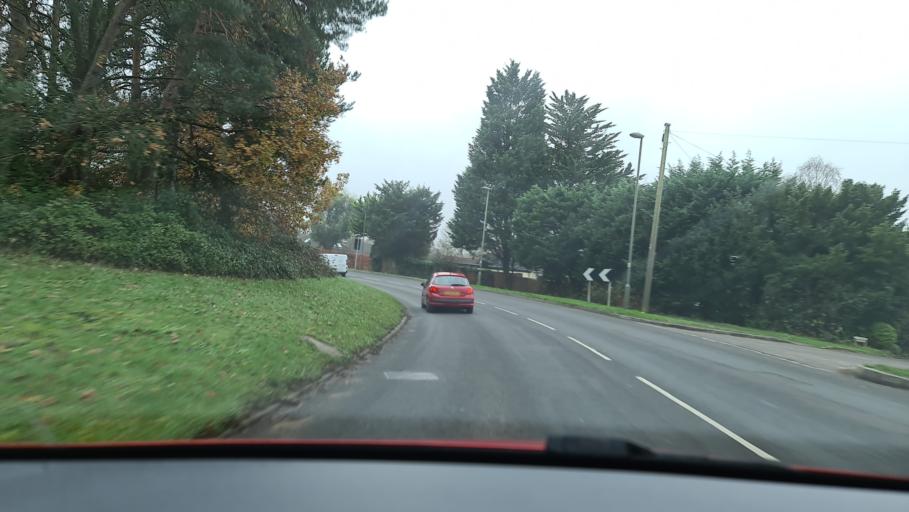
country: GB
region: England
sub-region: Surrey
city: Leatherhead
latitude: 51.3267
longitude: -0.3546
